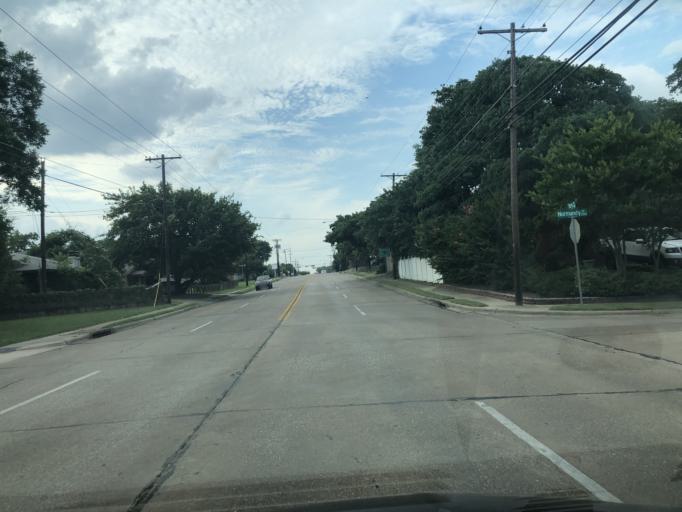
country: US
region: Texas
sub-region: Dallas County
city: Irving
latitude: 32.7979
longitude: -96.9771
